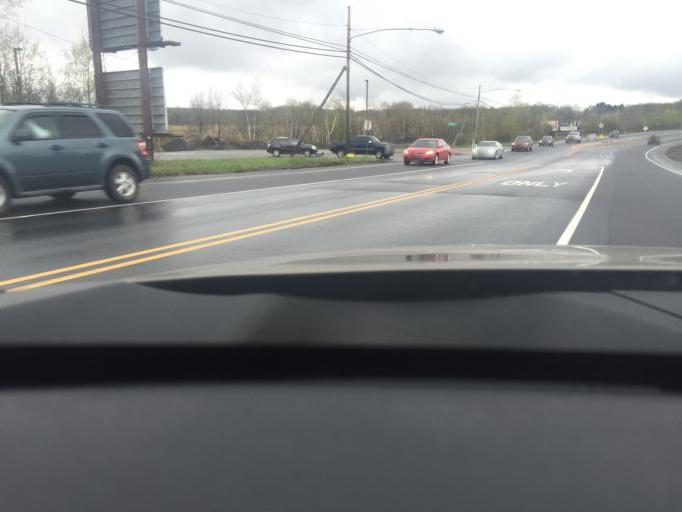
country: US
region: Pennsylvania
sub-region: Luzerne County
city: Harleigh
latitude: 40.9956
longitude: -75.9852
